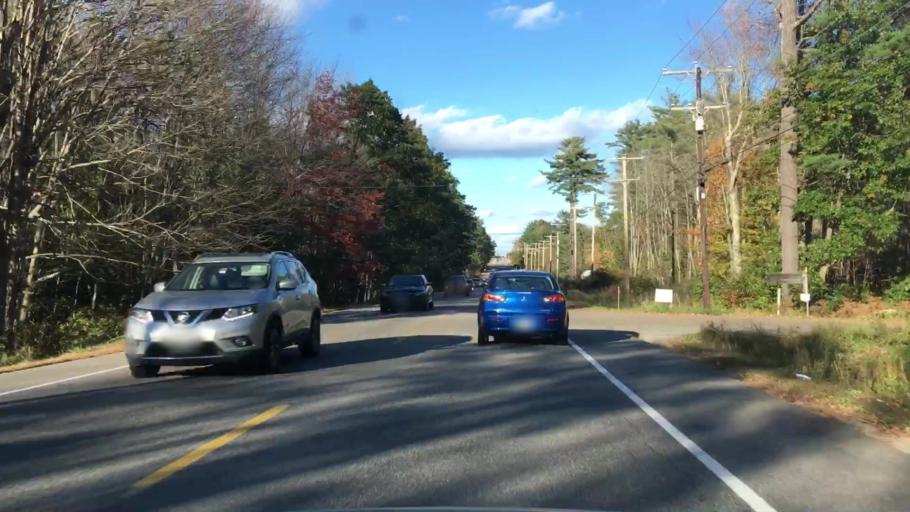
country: US
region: Maine
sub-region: Cumberland County
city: South Portland Gardens
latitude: 43.6140
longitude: -70.3569
